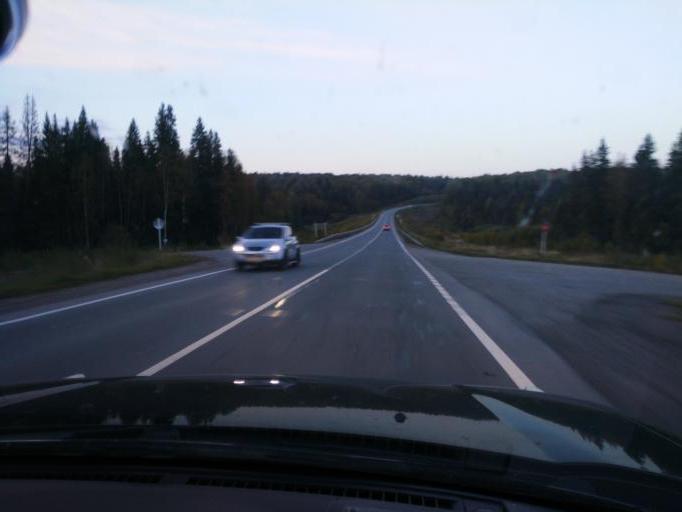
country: RU
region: Perm
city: Sylva
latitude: 58.2997
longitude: 56.7715
